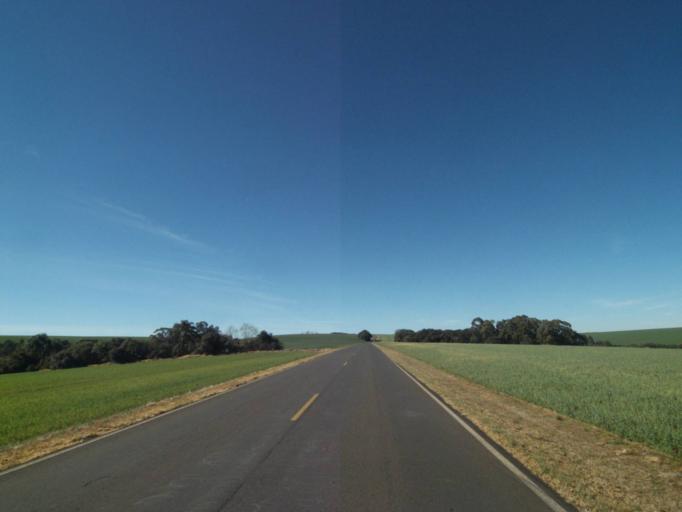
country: BR
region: Parana
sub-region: Tibagi
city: Tibagi
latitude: -24.5318
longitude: -50.3181
